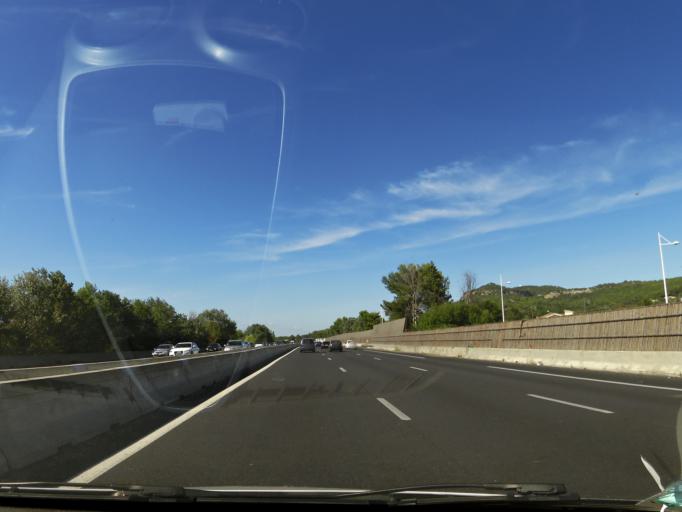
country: FR
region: Provence-Alpes-Cote d'Azur
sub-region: Departement du Vaucluse
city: Bollene
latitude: 44.3012
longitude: 4.7469
